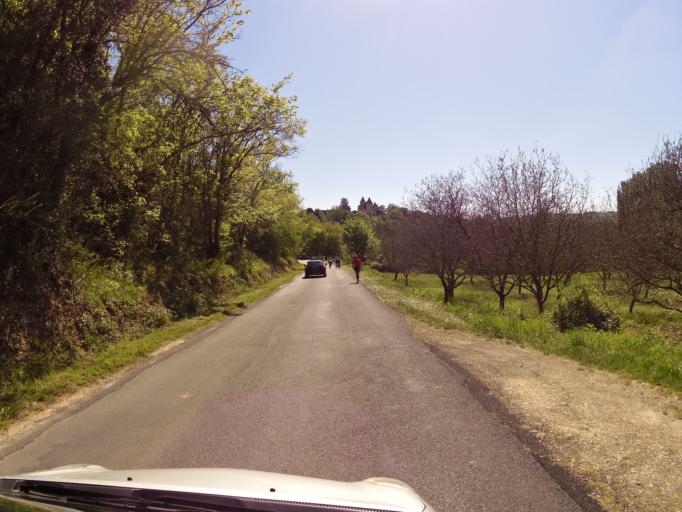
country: FR
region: Aquitaine
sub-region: Departement de la Dordogne
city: Saint-Cyprien
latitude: 44.8282
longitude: 1.1187
